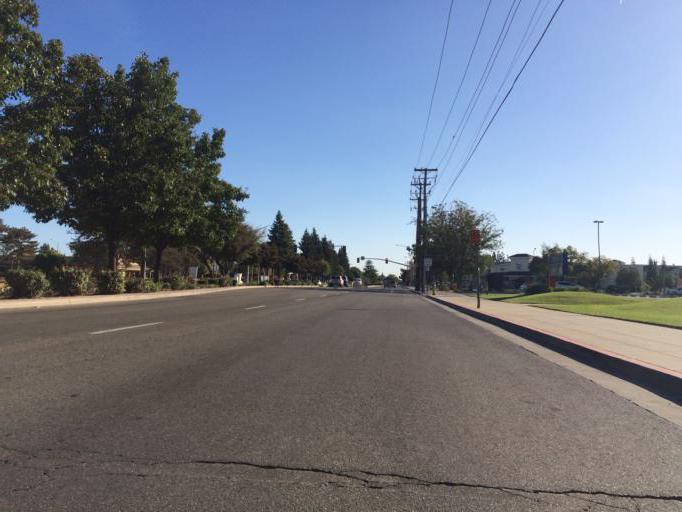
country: US
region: California
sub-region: Fresno County
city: Tarpey Village
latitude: 36.8097
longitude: -119.6821
